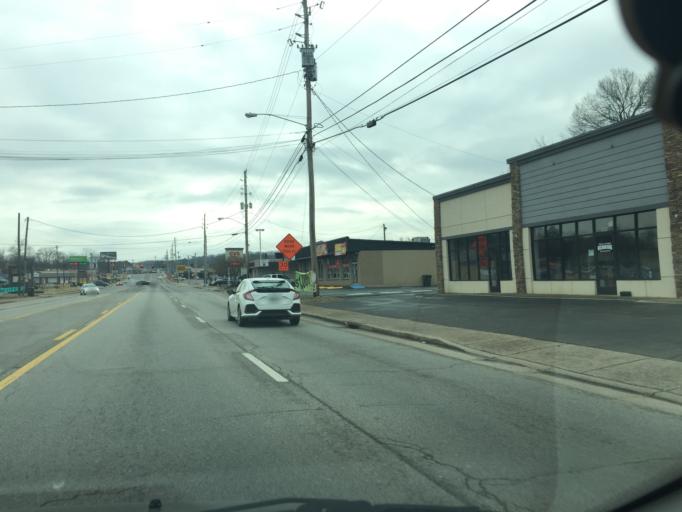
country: US
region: Tennessee
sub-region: Hamilton County
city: East Brainerd
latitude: 35.0047
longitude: -85.1515
